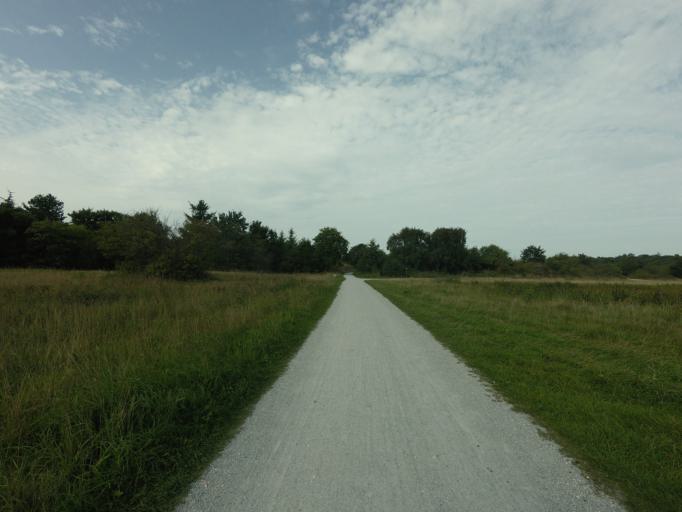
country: NL
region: Friesland
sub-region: Gemeente Schiermonnikoog
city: Schiermonnikoog
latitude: 53.4832
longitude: 6.1594
